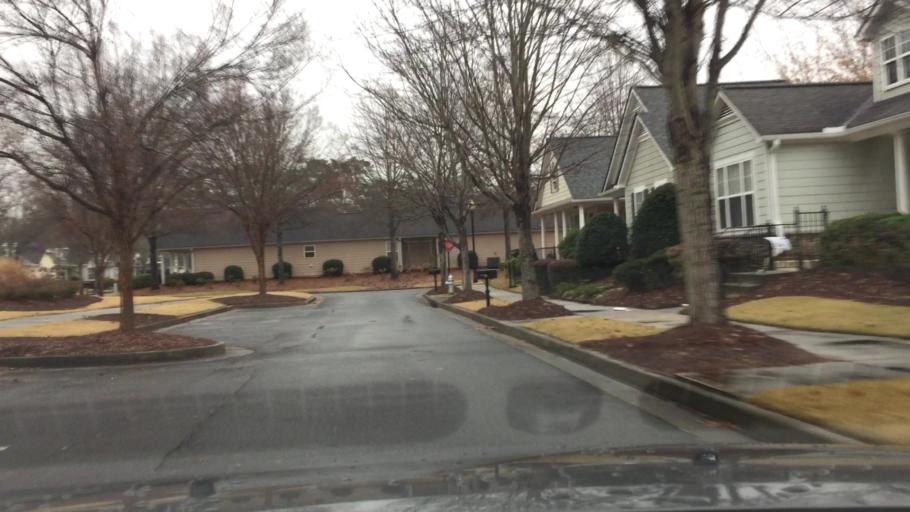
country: US
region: Georgia
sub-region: Cobb County
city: Powder Springs
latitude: 33.8650
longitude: -84.6885
